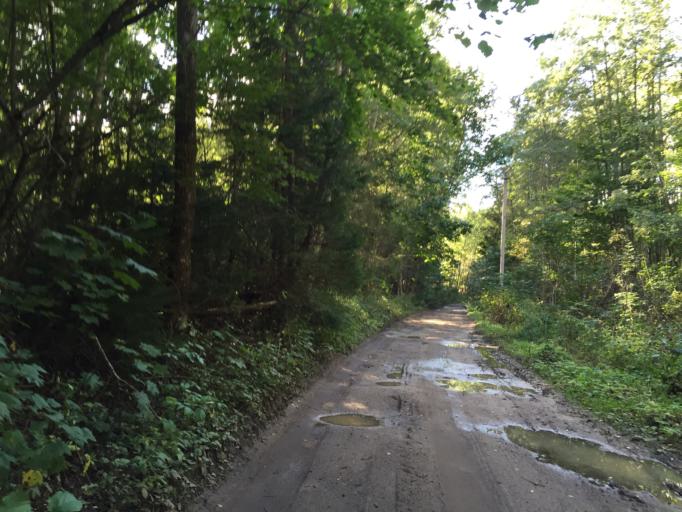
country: LV
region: Kuldigas Rajons
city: Kuldiga
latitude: 57.0076
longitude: 21.7849
